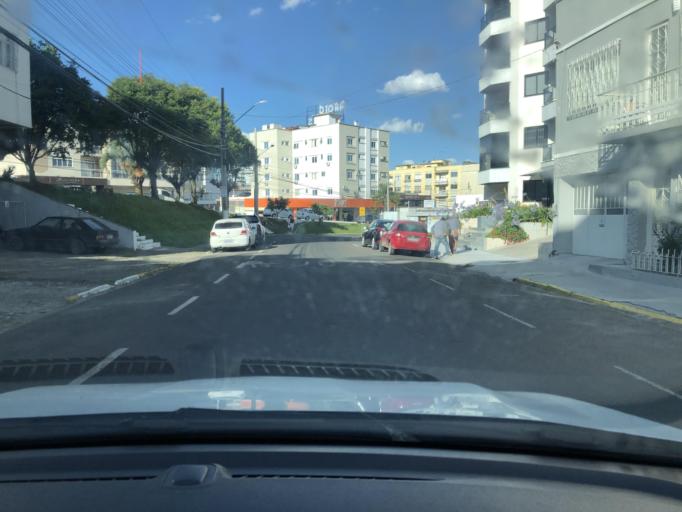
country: BR
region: Santa Catarina
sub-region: Lages
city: Lages
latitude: -27.8111
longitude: -50.3213
